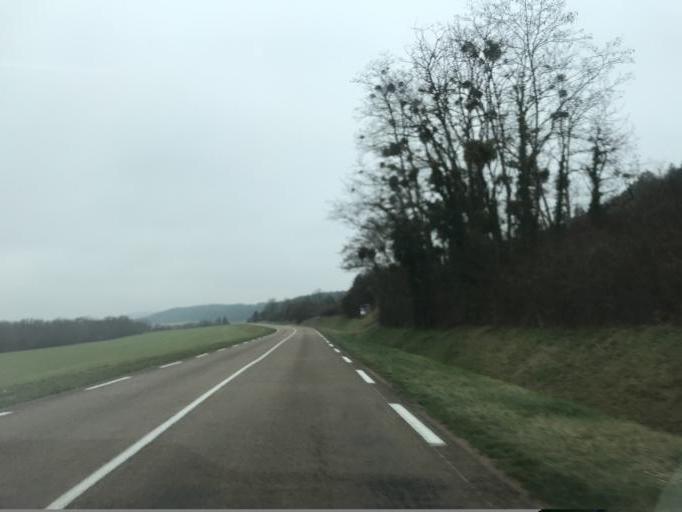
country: FR
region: Bourgogne
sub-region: Departement de l'Yonne
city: Avallon
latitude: 47.5139
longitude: 3.7673
